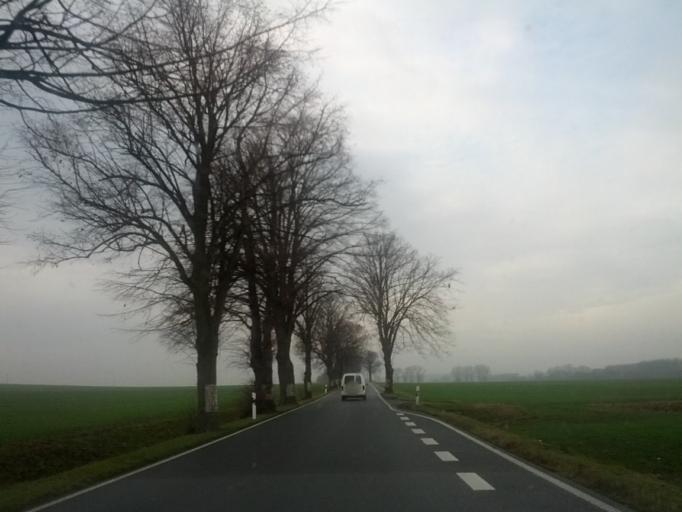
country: DE
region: Thuringia
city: Goldbach
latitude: 50.9999
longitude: 10.6425
